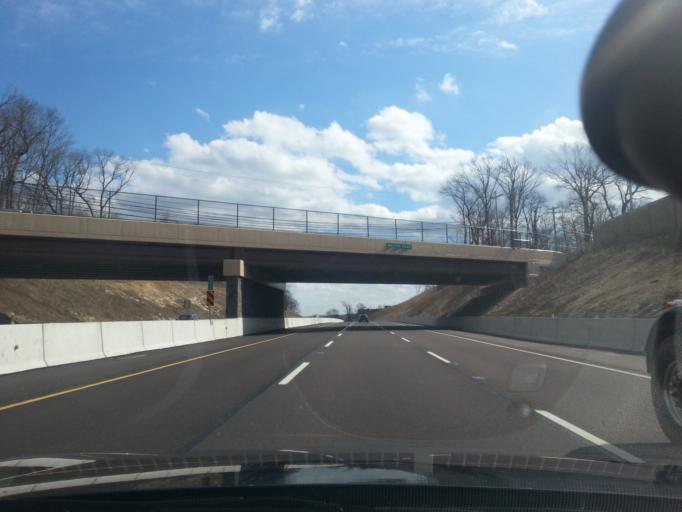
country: US
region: Pennsylvania
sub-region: Montgomery County
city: Plymouth Meeting
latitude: 40.1268
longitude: -75.2844
